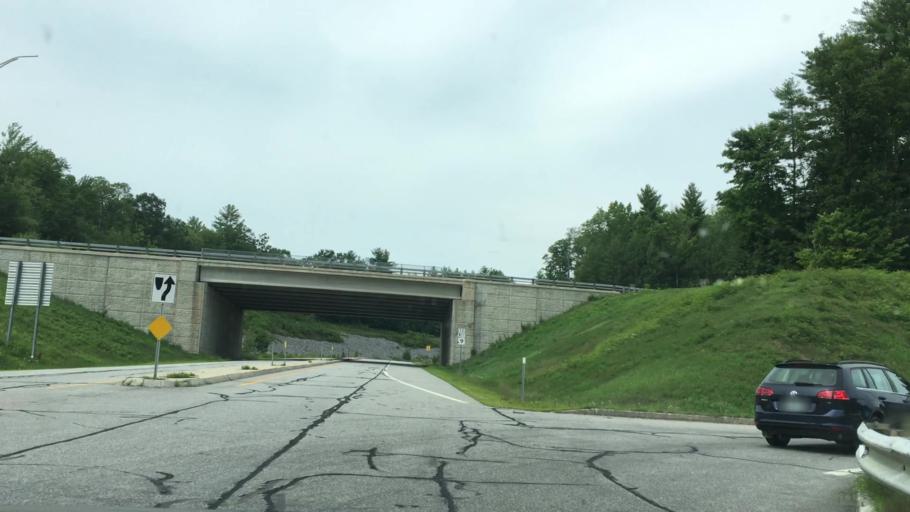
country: US
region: New Hampshire
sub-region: Hillsborough County
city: Hillsborough
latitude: 43.1156
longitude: -71.9180
